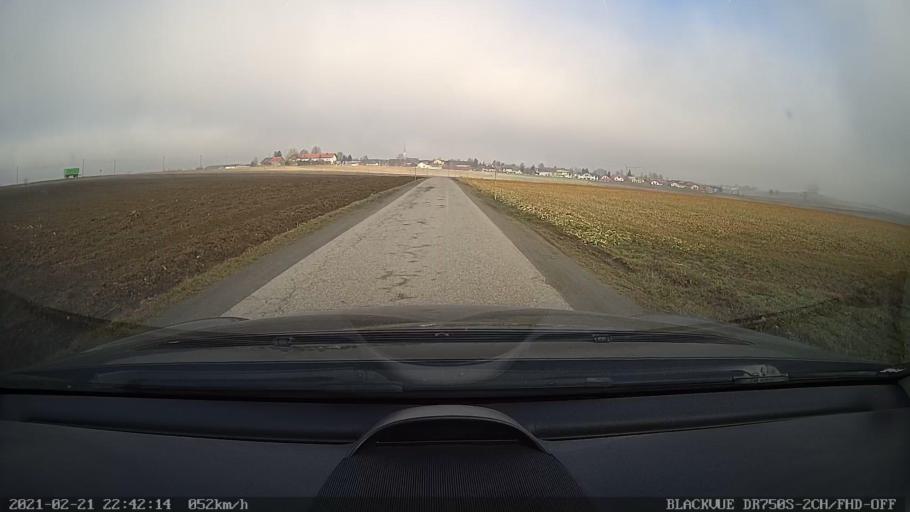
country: DE
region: Bavaria
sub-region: Upper Bavaria
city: Griesstatt
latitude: 47.9835
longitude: 12.1805
